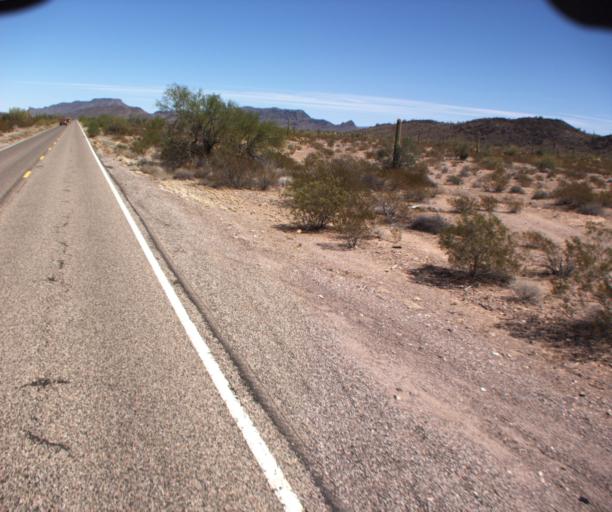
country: US
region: Arizona
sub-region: Pima County
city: Ajo
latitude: 32.2305
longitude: -112.7535
